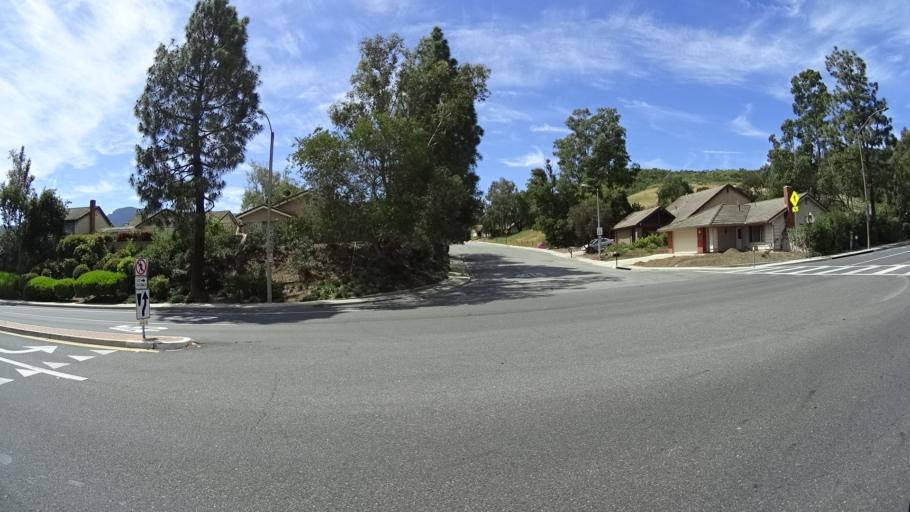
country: US
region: California
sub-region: Ventura County
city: Casa Conejo
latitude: 34.1789
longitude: -118.9587
